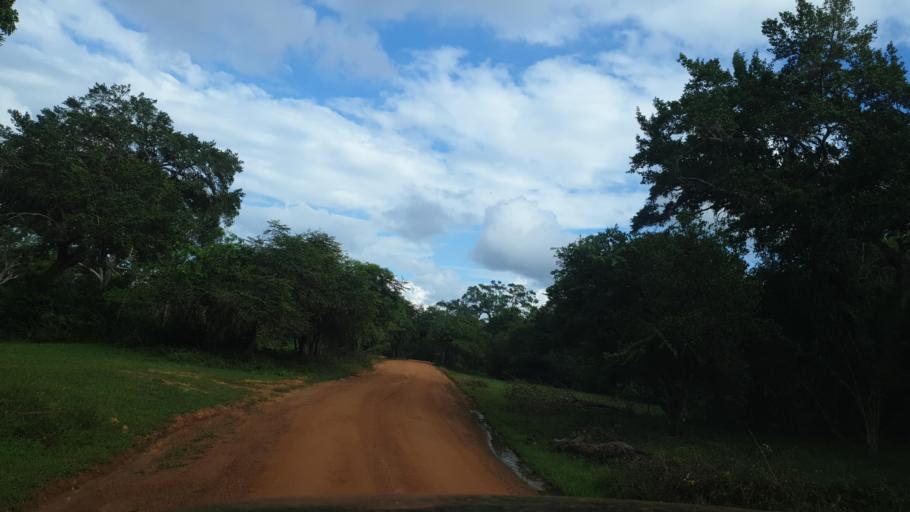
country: LK
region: North Central
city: Anuradhapura
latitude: 8.3636
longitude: 80.0995
